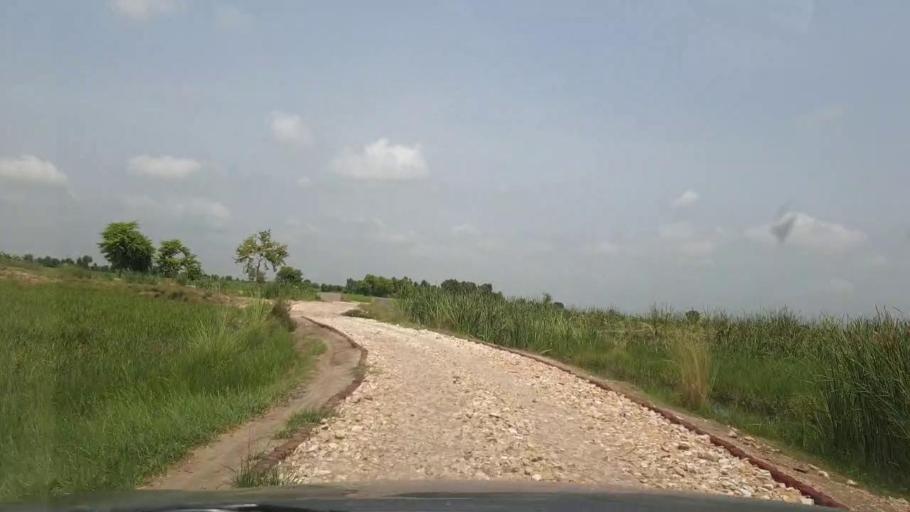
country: PK
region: Sindh
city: Ratodero
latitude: 27.9204
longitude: 68.3064
